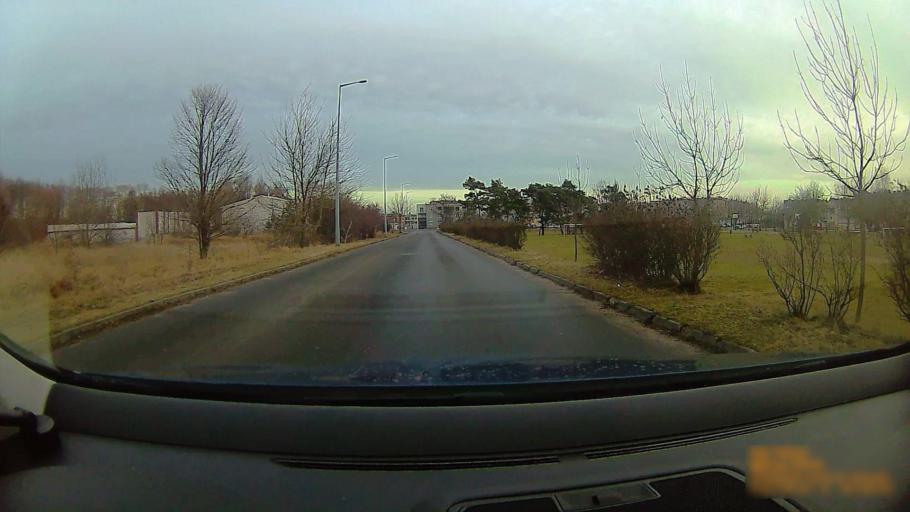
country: PL
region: Greater Poland Voivodeship
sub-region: Konin
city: Konin
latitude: 52.2353
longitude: 18.2184
